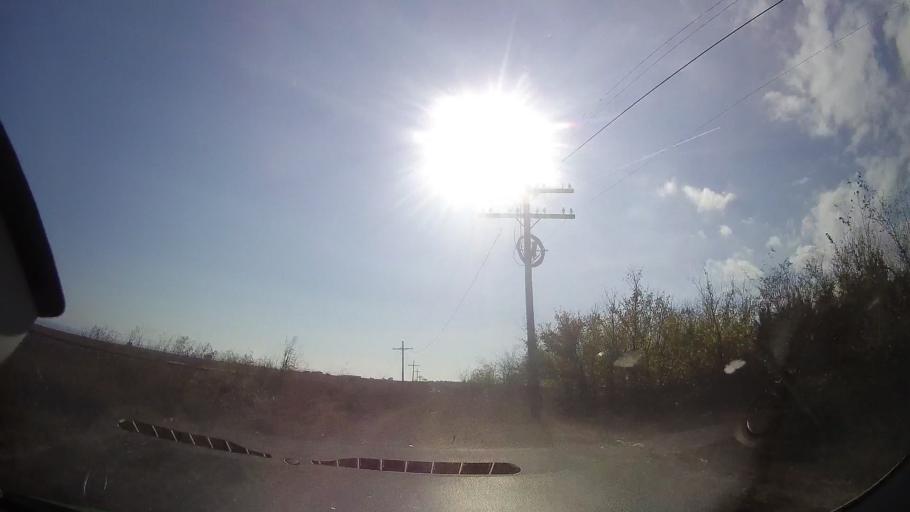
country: RO
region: Constanta
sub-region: Comuna Tuzla
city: Tuzla
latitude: 43.9837
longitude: 28.6447
